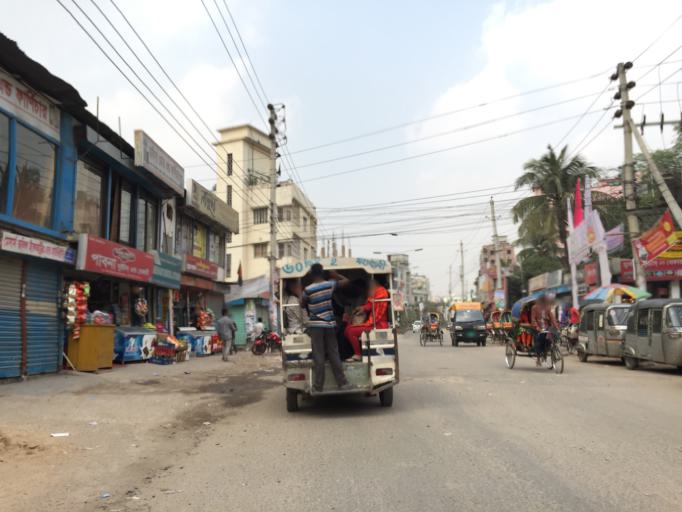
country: BD
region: Dhaka
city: Azimpur
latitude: 23.7852
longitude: 90.3674
